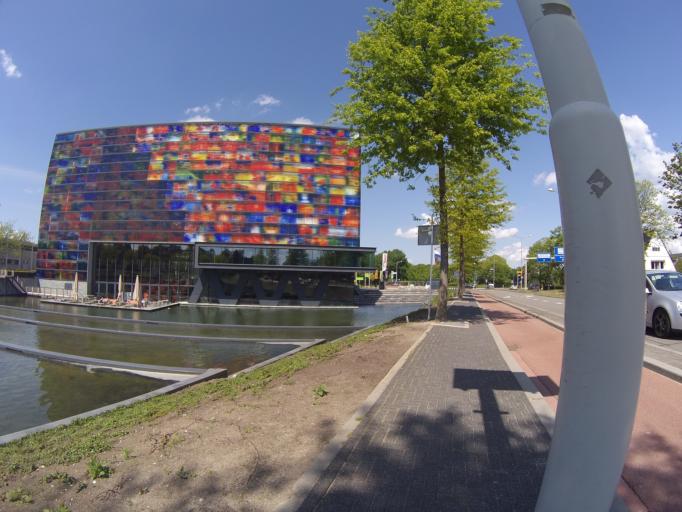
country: NL
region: North Holland
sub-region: Gemeente Hilversum
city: Hilversum
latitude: 52.2349
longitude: 5.1737
